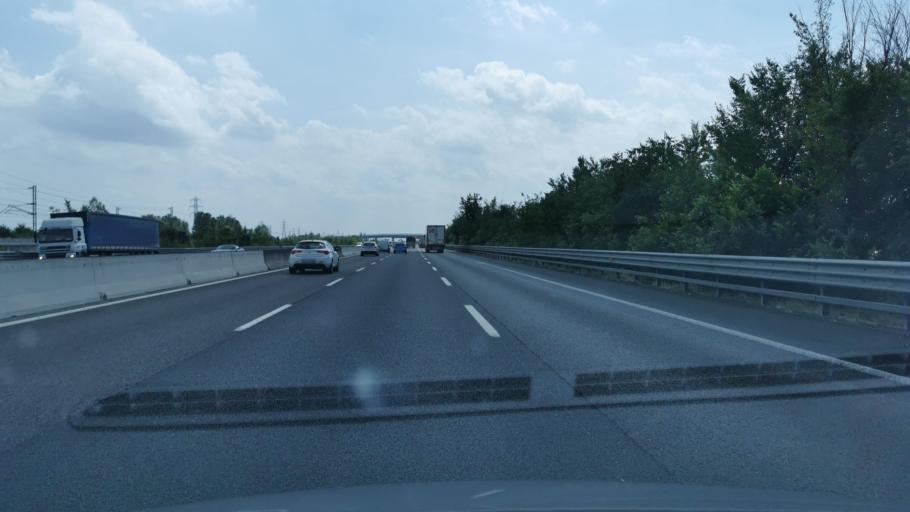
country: IT
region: Emilia-Romagna
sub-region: Provincia di Reggio Emilia
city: Praticello
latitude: 44.7957
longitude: 10.4635
